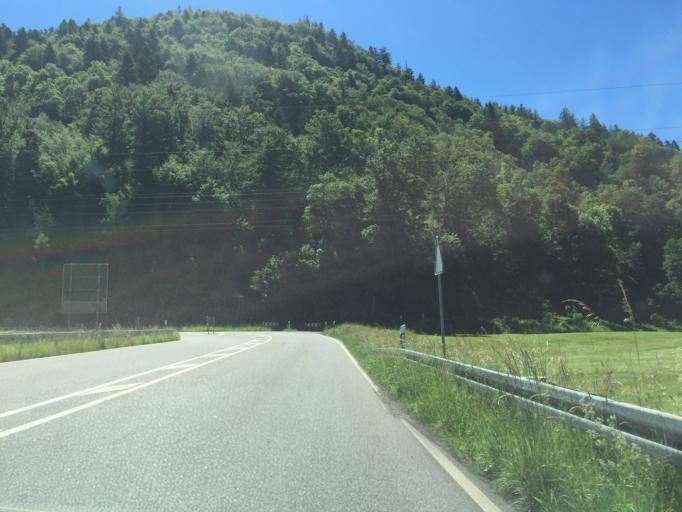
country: DE
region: Baden-Wuerttemberg
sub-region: Freiburg Region
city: Aitern
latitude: 47.7981
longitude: 7.9057
